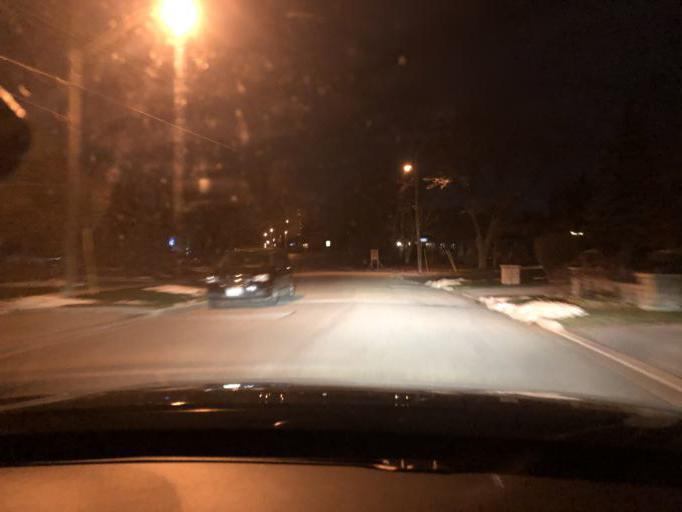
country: CA
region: Ontario
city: Scarborough
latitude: 43.7742
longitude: -79.3024
